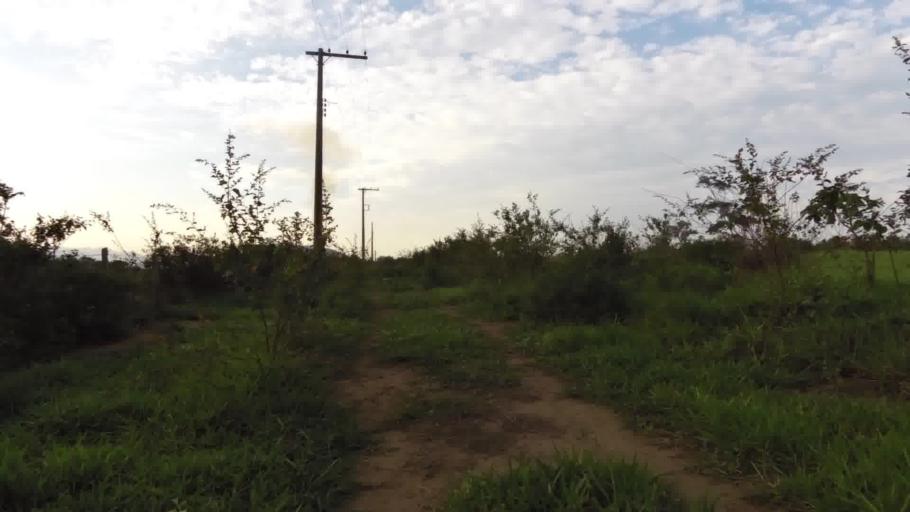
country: BR
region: Espirito Santo
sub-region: Piuma
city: Piuma
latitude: -20.8294
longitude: -40.7348
